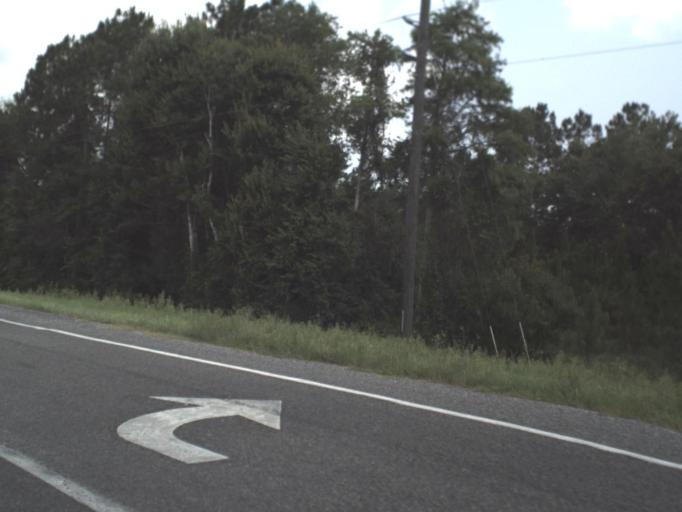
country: US
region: Florida
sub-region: Levy County
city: Bronson
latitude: 29.4765
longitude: -82.6835
